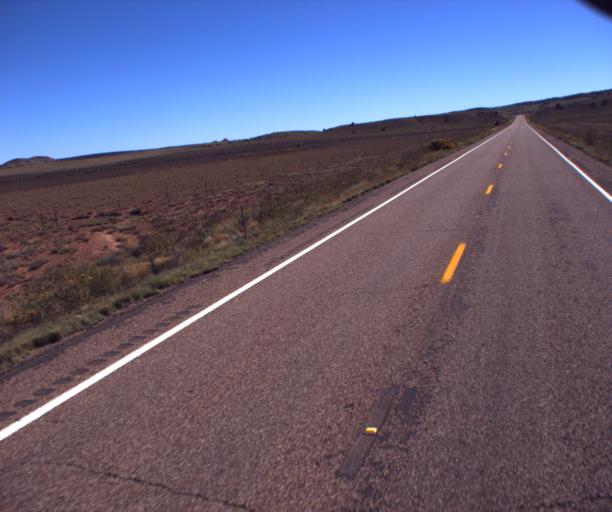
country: US
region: Arizona
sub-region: Apache County
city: Saint Johns
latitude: 34.5896
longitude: -109.5975
